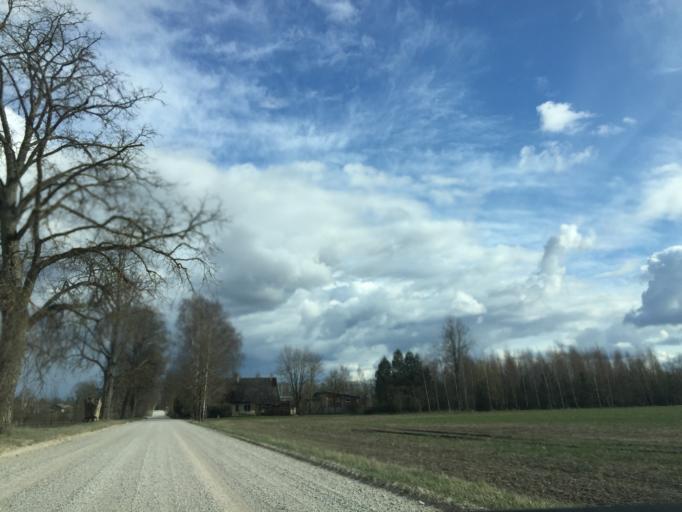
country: LV
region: Burtnieki
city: Matisi
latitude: 57.6022
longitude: 25.0860
